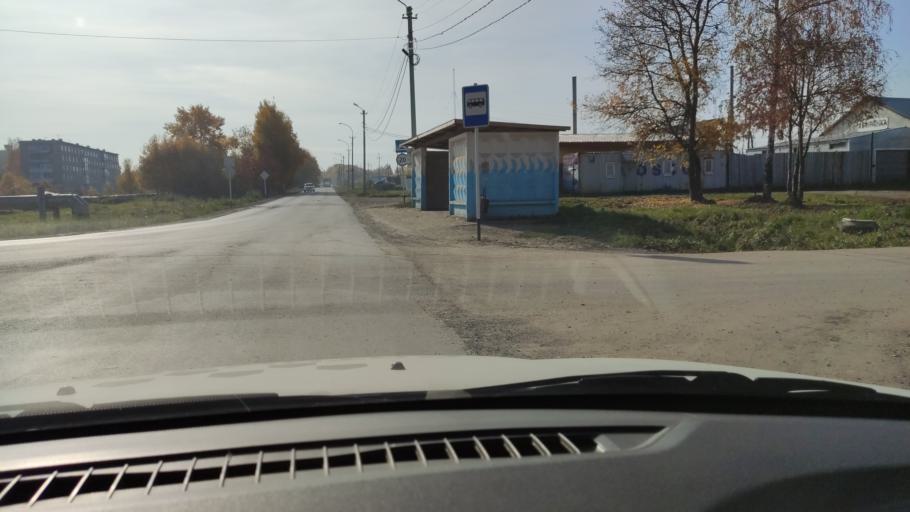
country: RU
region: Perm
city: Sylva
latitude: 58.0305
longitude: 56.7407
